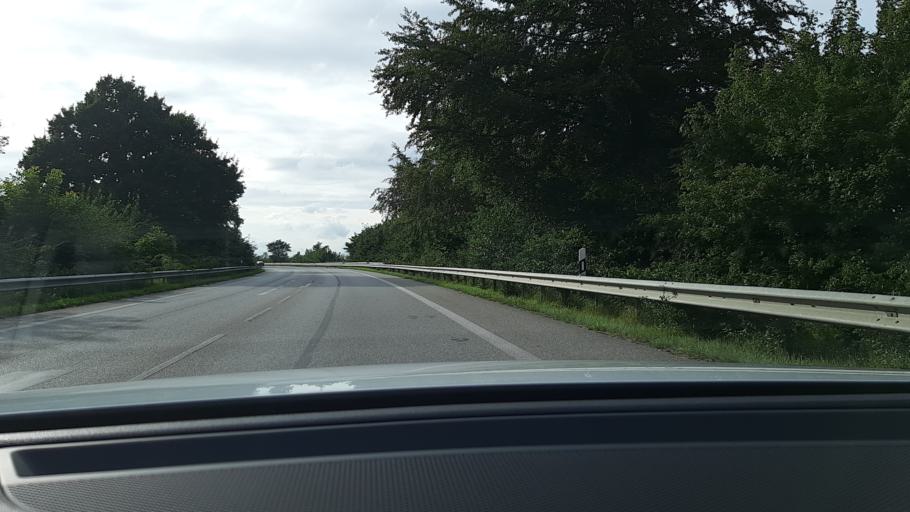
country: DE
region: Schleswig-Holstein
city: Stockelsdorf
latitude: 53.8918
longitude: 10.6346
